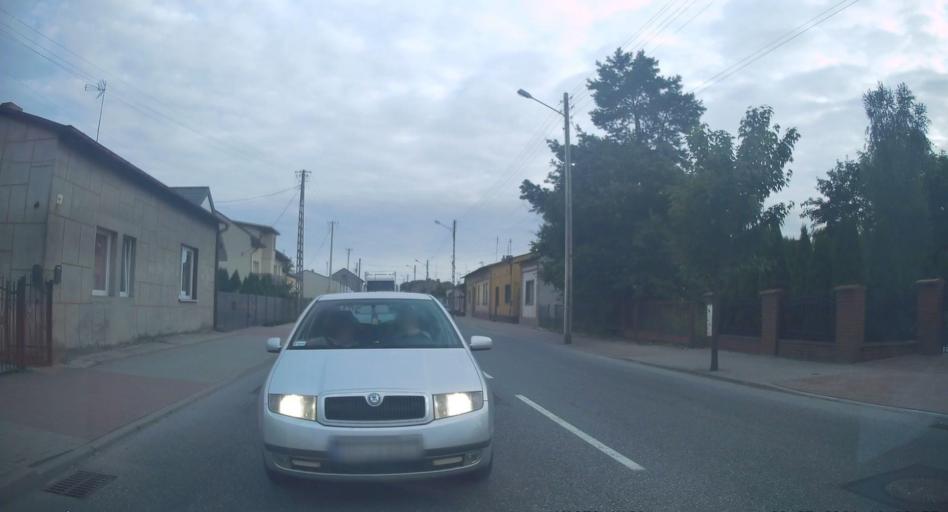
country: PL
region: Lodz Voivodeship
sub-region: Powiat radomszczanski
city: Kamiensk
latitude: 51.1948
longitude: 19.4987
